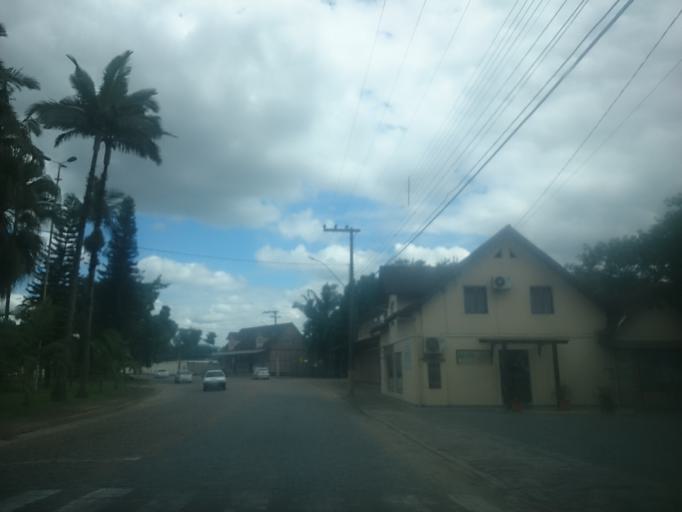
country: BR
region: Santa Catarina
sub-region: Pomerode
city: Pomerode
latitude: -26.7065
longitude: -49.1644
